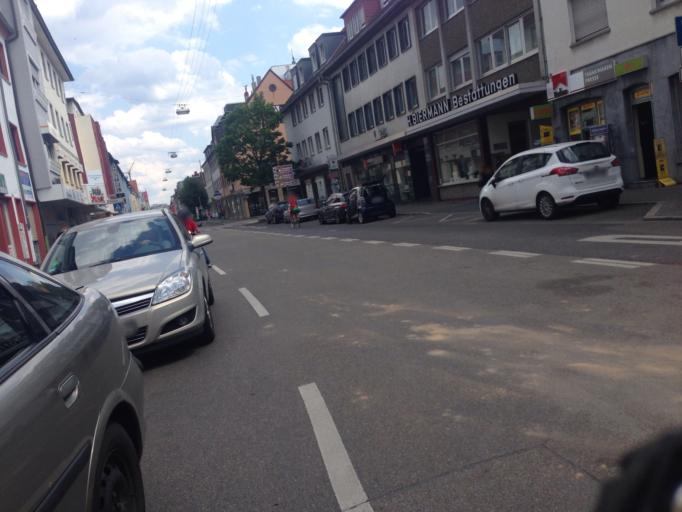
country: DE
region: Hesse
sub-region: Regierungsbezirk Darmstadt
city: Hanau am Main
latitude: 50.1324
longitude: 8.9126
